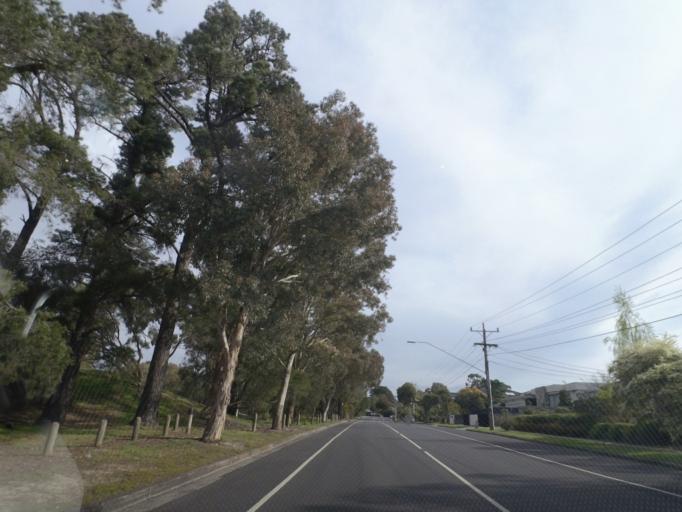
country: AU
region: Victoria
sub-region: Knox
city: Wantirna
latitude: -37.8524
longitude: 145.2029
